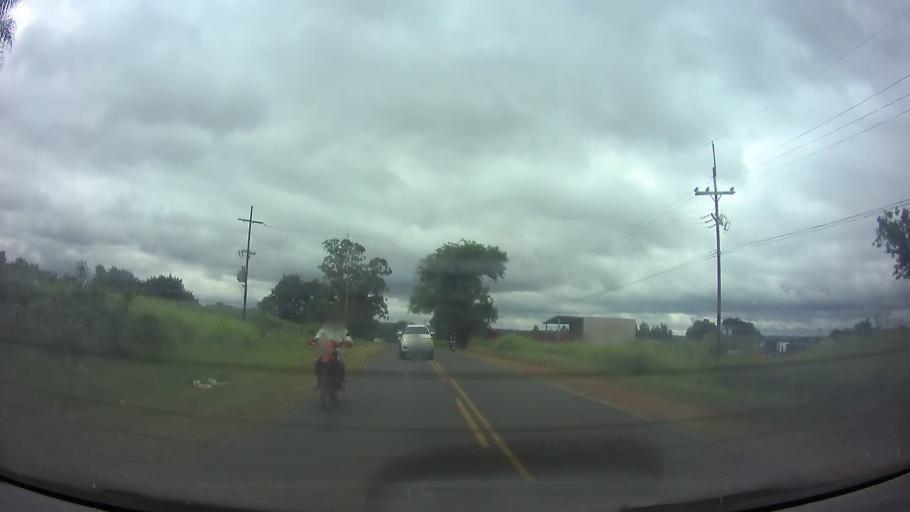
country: PY
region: Central
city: Guarambare
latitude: -25.5076
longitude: -57.4853
